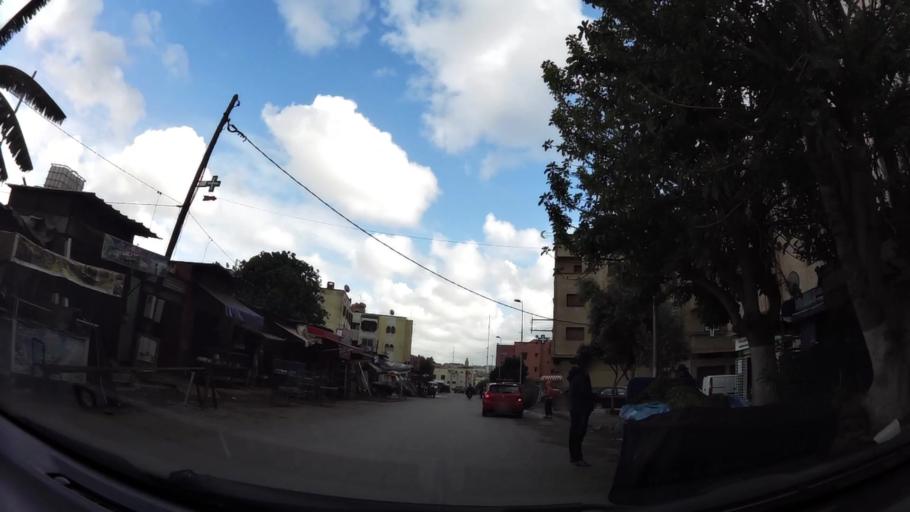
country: MA
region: Grand Casablanca
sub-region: Casablanca
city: Casablanca
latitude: 33.5458
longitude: -7.5869
